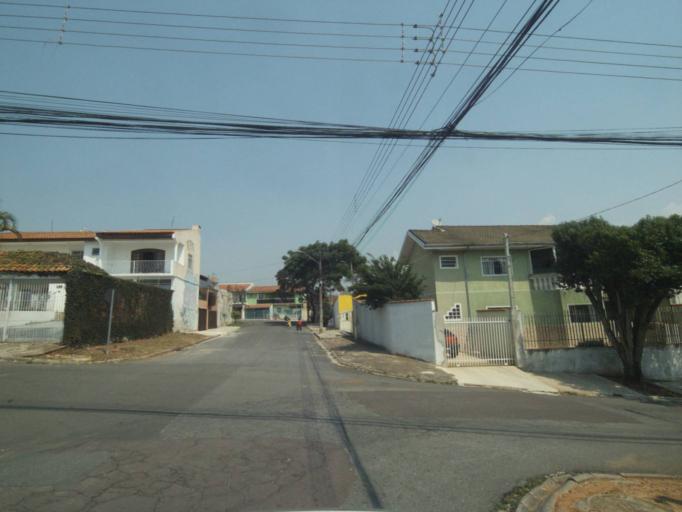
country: BR
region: Parana
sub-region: Sao Jose Dos Pinhais
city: Sao Jose dos Pinhais
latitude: -25.5440
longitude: -49.2442
